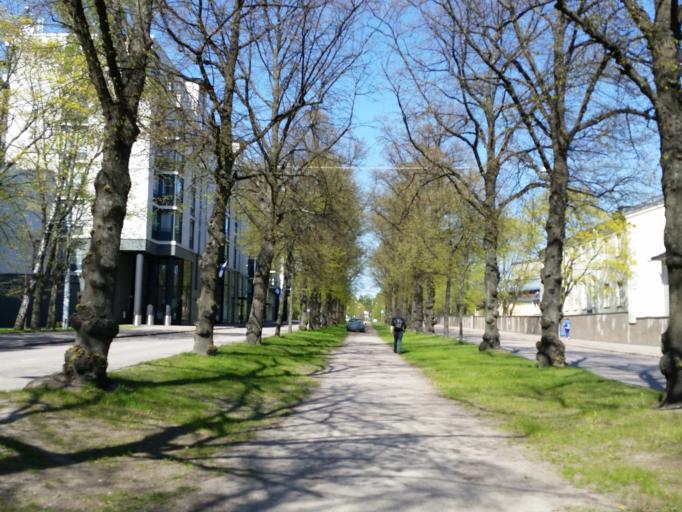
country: FI
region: Uusimaa
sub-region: Helsinki
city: Helsinki
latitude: 60.1782
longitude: 24.9170
